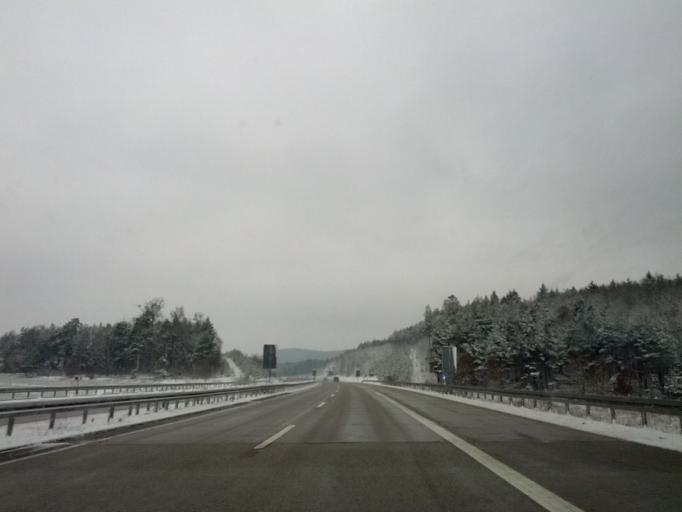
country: DE
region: Thuringia
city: Wolfershausen
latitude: 50.4643
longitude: 10.4540
